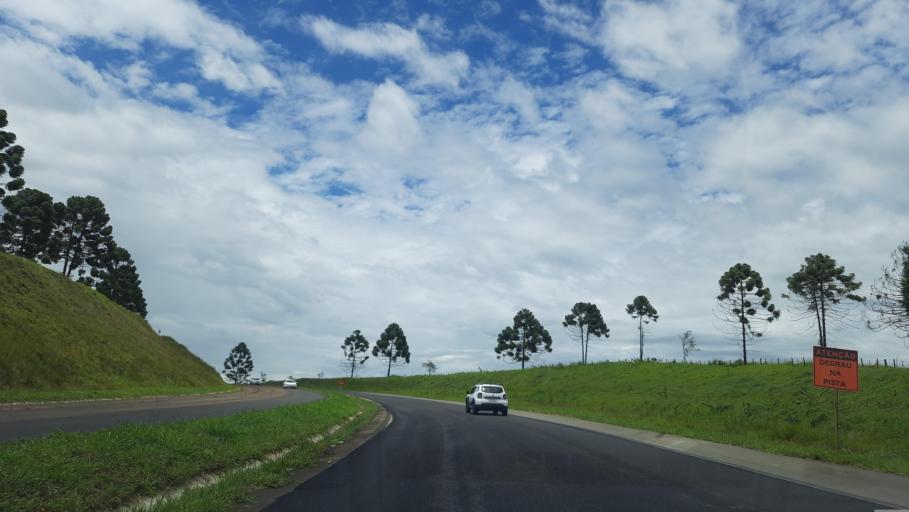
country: BR
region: Minas Gerais
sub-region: Pocos De Caldas
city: Pocos de Caldas
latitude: -21.8346
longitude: -46.6705
